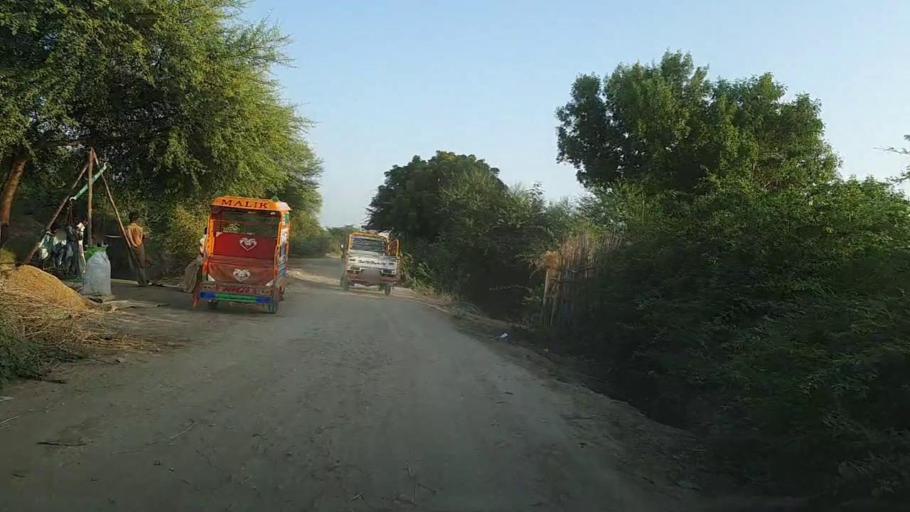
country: PK
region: Sindh
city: Kario
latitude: 24.6930
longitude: 68.6721
